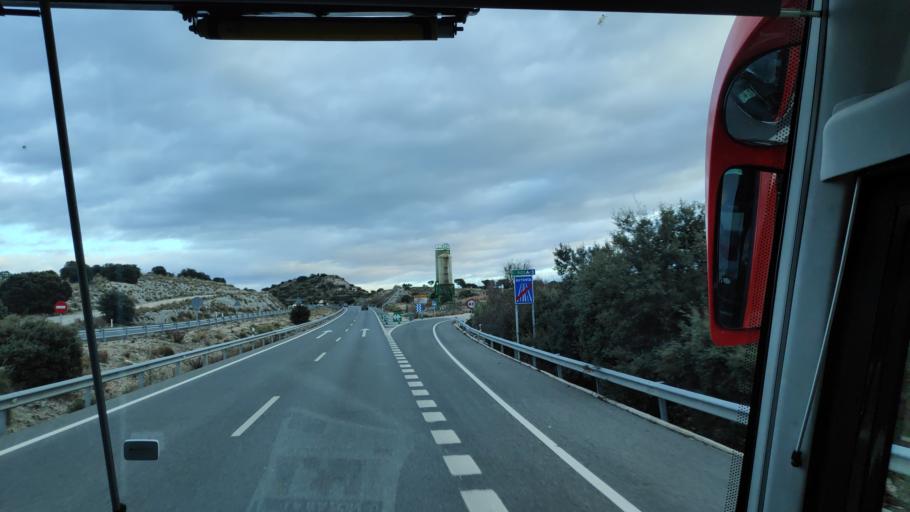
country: ES
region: Madrid
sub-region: Provincia de Madrid
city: Villarejo de Salvanes
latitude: 40.1445
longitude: -3.2145
